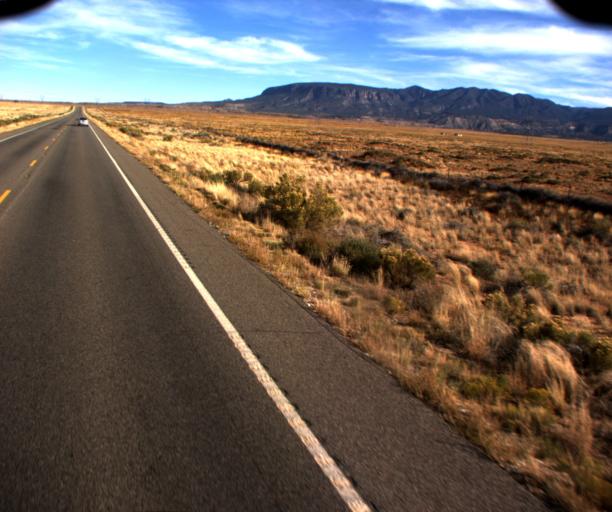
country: US
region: Arizona
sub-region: Apache County
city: Lukachukai
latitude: 36.9425
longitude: -109.2573
